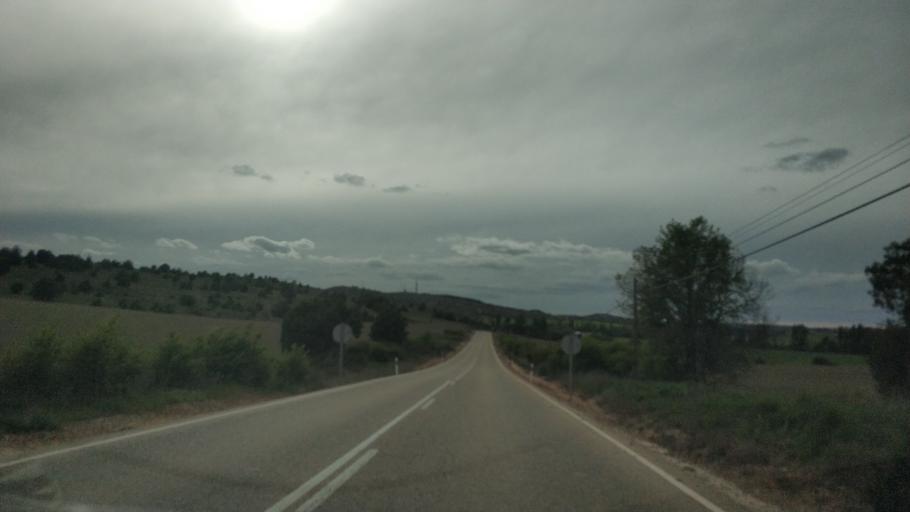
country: ES
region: Castille and Leon
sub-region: Provincia de Soria
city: El Burgo de Osma
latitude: 41.5763
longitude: -3.0273
